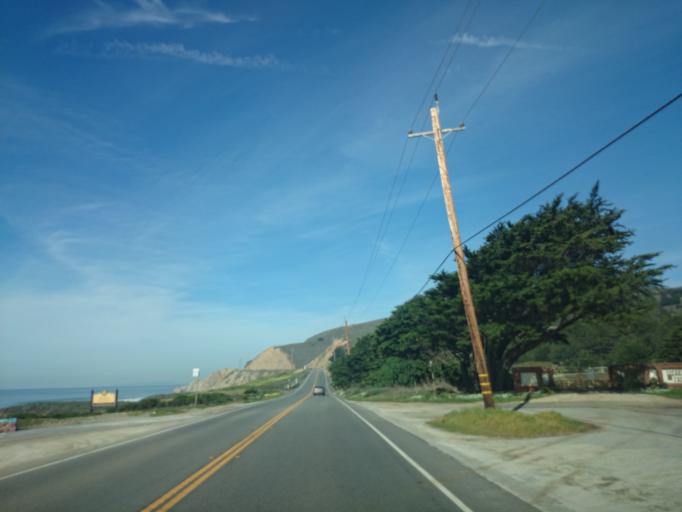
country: US
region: California
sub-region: San Mateo County
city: Montara
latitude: 37.5516
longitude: -122.5121
